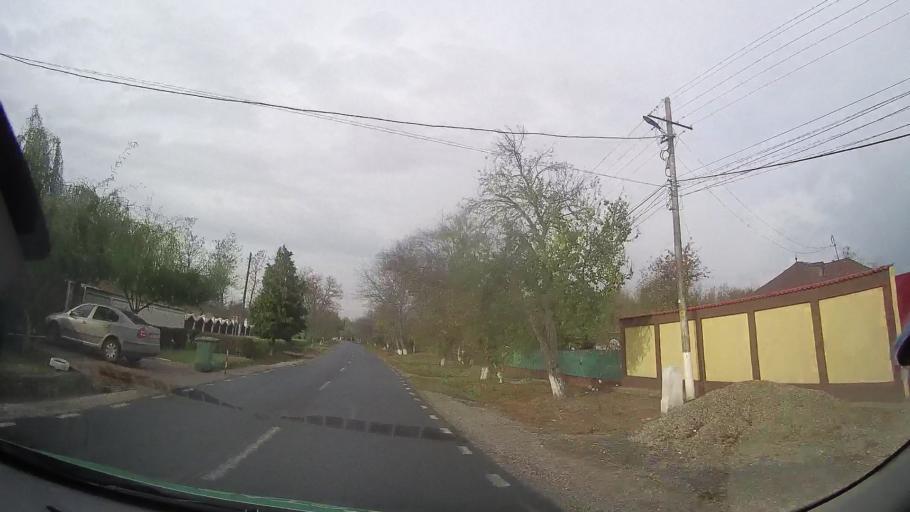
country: RO
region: Ialomita
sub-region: Comuna Fierbinti-Targ
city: Fierbinti-Targ
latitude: 44.7056
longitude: 26.3244
